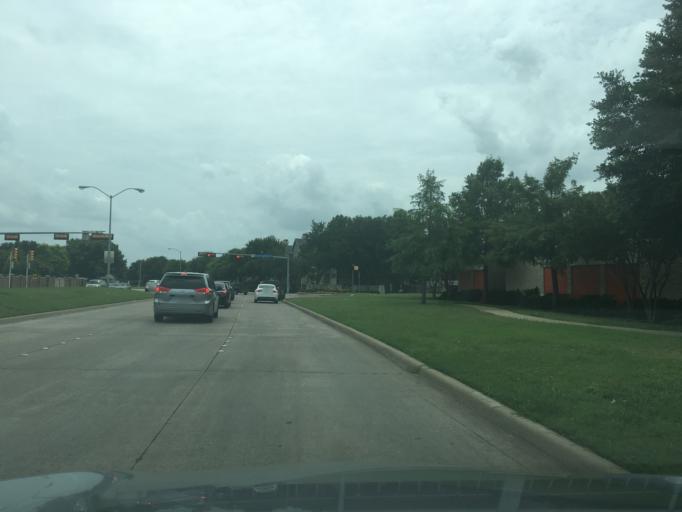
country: US
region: Texas
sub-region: Dallas County
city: Richardson
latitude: 32.9357
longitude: -96.7197
